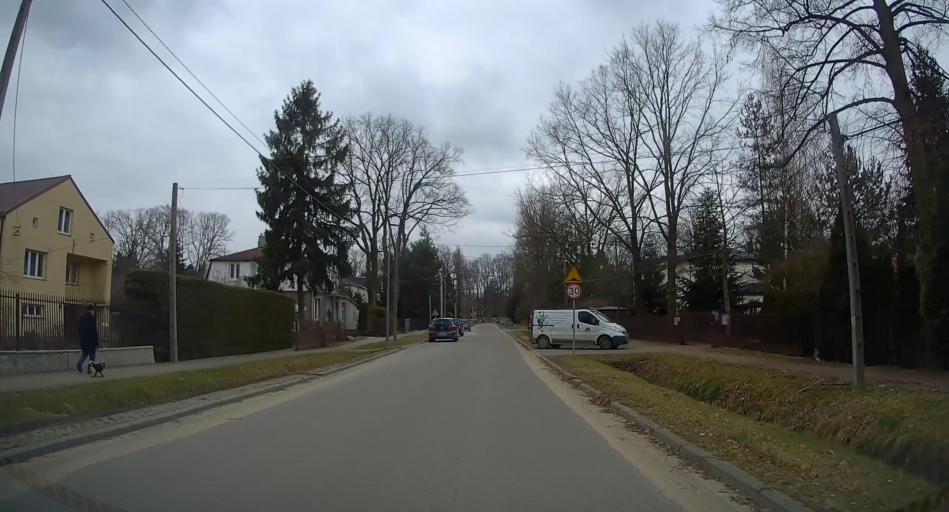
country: PL
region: Masovian Voivodeship
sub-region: Powiat piaseczynski
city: Piaseczno
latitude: 52.0609
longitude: 21.0016
